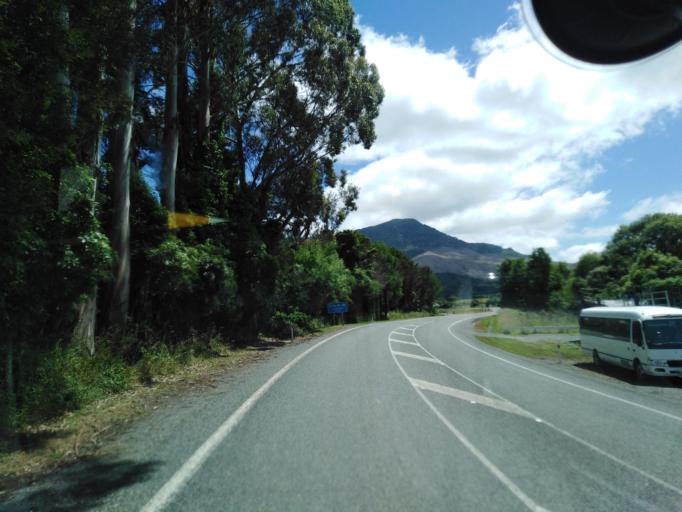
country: NZ
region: Nelson
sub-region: Nelson City
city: Nelson
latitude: -41.2157
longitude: 173.3952
